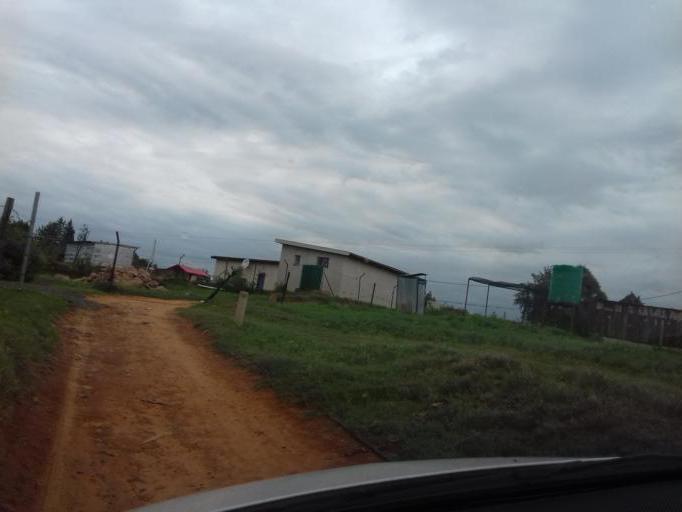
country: LS
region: Berea
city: Teyateyaneng
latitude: -29.1078
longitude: 27.9649
